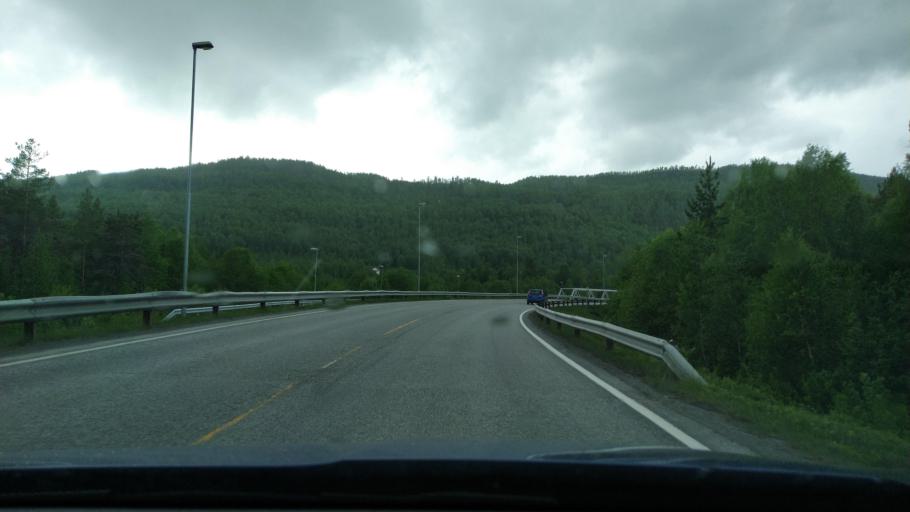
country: NO
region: Troms
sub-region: Malselv
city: Moen
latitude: 69.0103
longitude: 18.4906
